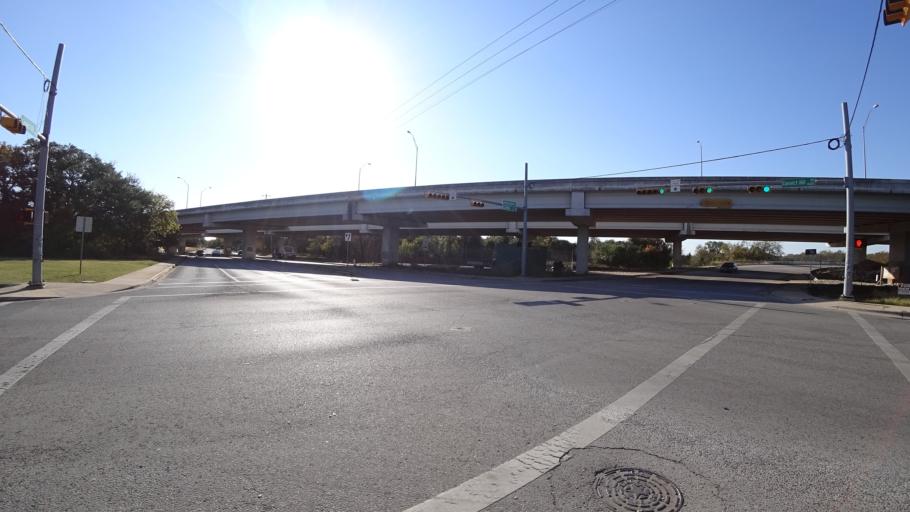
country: US
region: Texas
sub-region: Travis County
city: Shady Hollow
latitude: 30.2170
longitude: -97.8459
